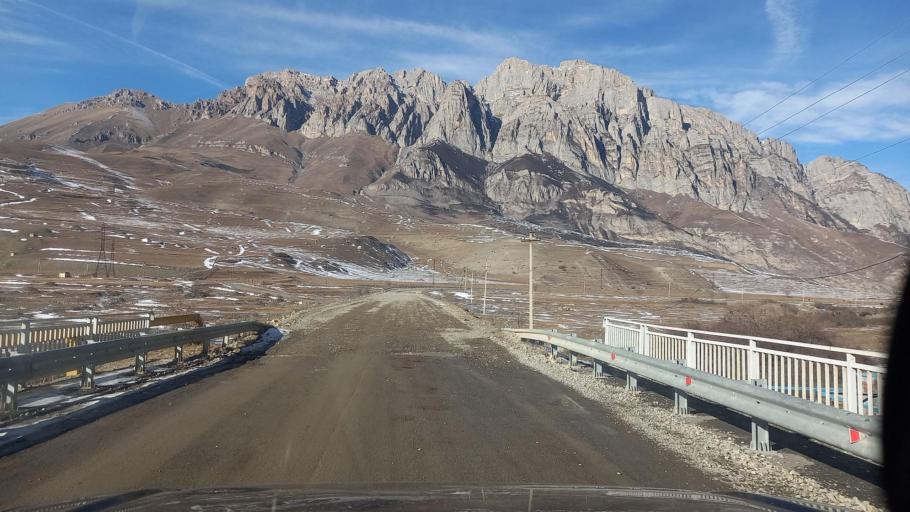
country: RU
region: North Ossetia
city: Verkhniy Fiagdon
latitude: 42.8411
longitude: 44.4441
